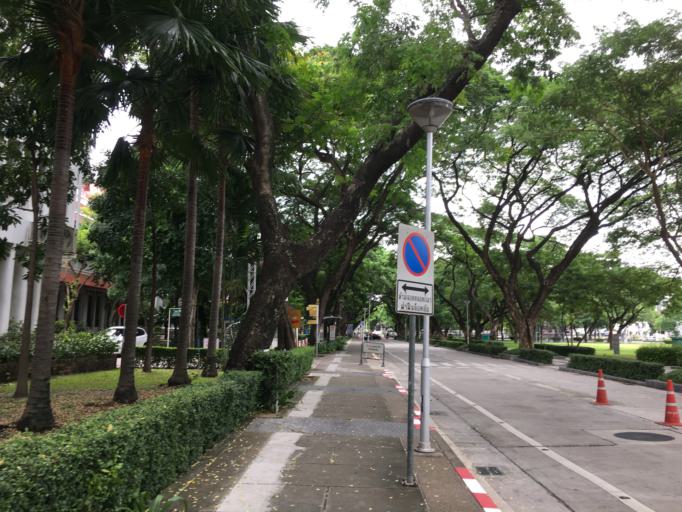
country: TH
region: Bangkok
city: Pathum Wan
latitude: 13.7376
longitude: 100.5316
